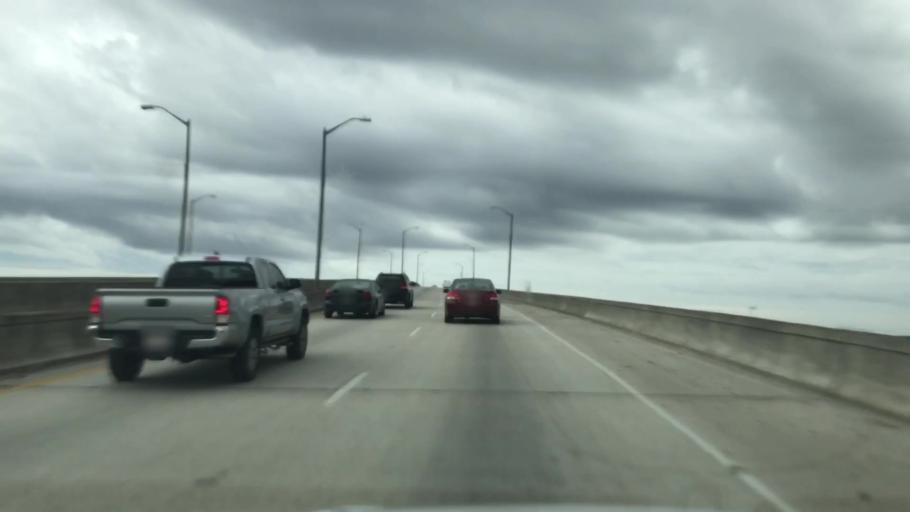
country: US
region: South Carolina
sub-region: Georgetown County
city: Georgetown
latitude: 33.3611
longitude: -79.2954
